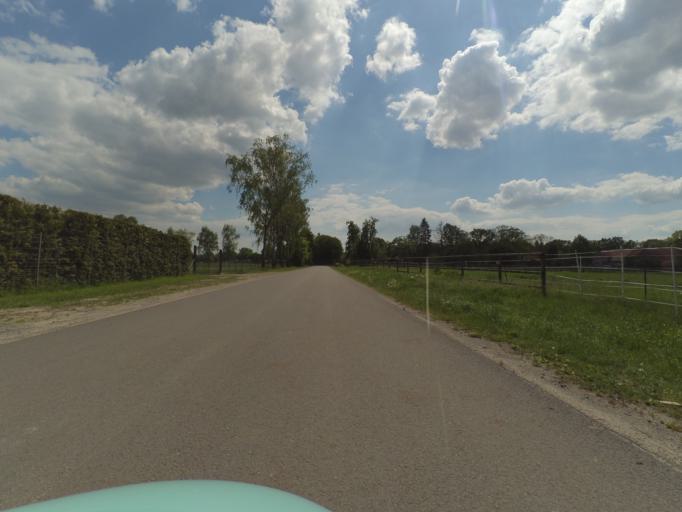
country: DE
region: Lower Saxony
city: Ummern
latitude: 52.5525
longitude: 10.4061
